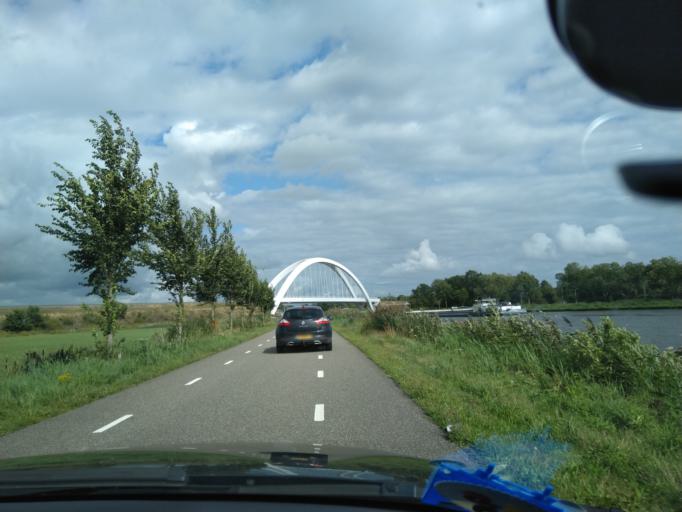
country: NL
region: Groningen
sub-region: Gemeente Zuidhorn
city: Noordhorn
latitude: 53.2531
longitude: 6.3859
